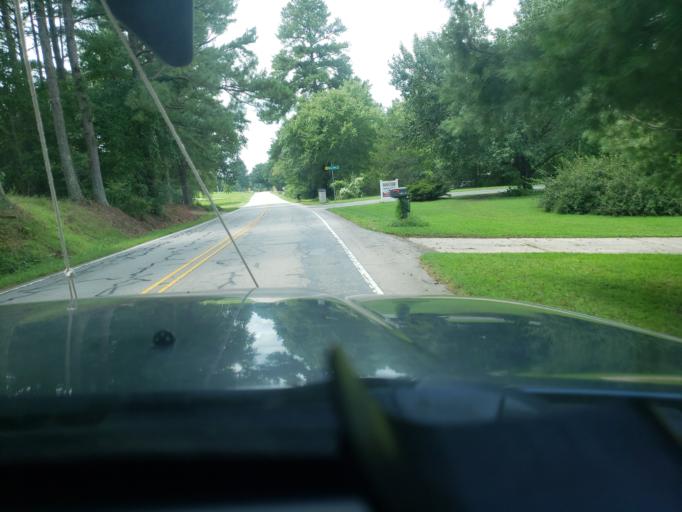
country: US
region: North Carolina
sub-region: Wake County
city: Rolesville
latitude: 35.8793
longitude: -78.4700
